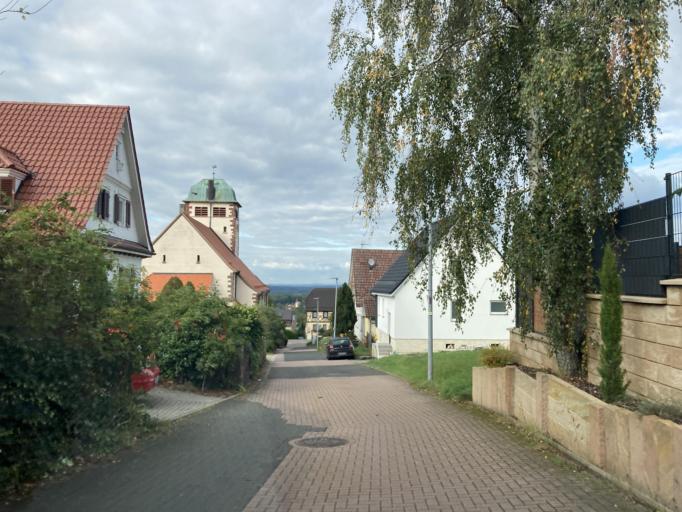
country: DE
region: Baden-Wuerttemberg
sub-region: Karlsruhe Region
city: Dobel
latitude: 48.8417
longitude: 8.5314
